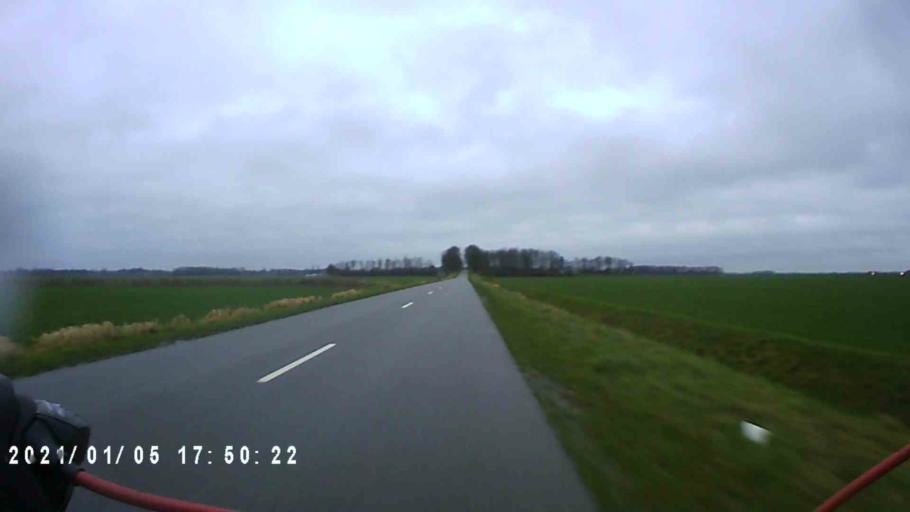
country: NL
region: Groningen
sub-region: Gemeente Slochteren
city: Slochteren
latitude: 53.2054
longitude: 6.8940
